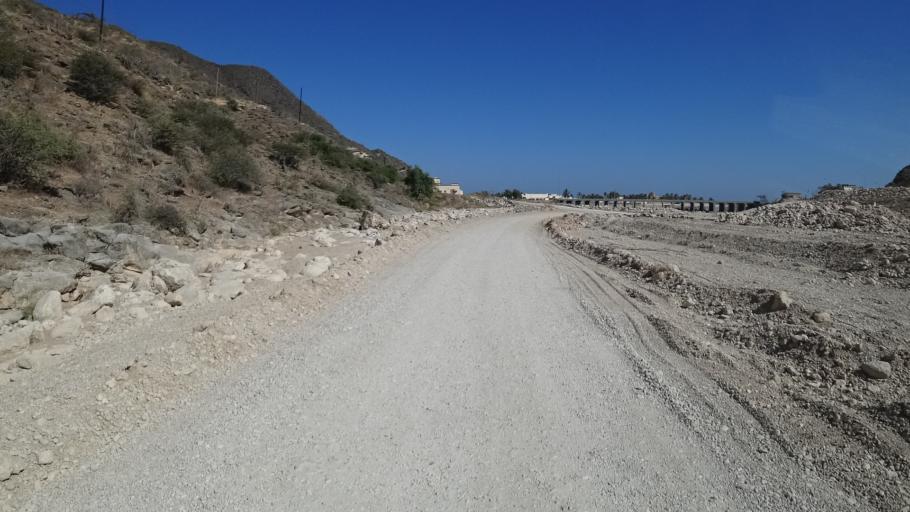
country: YE
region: Al Mahrah
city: Hawf
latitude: 16.7505
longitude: 53.4179
